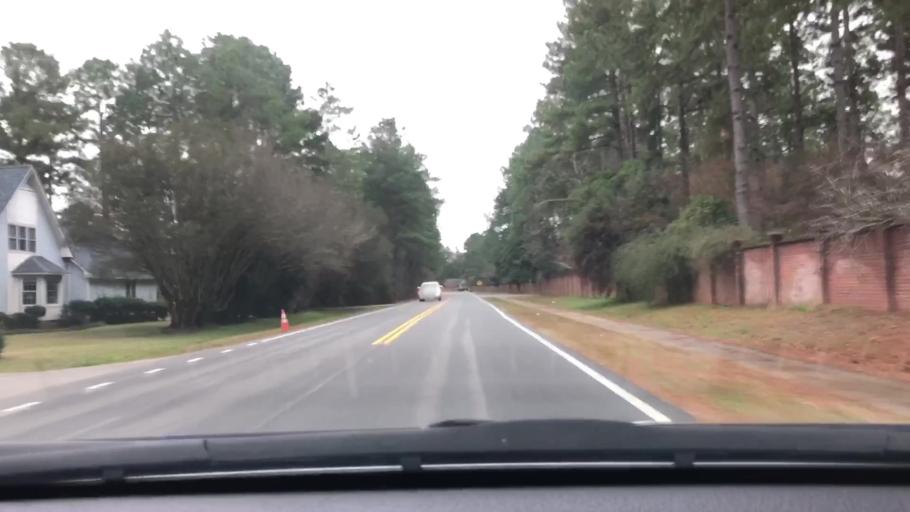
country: US
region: South Carolina
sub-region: Sumter County
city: Cherryvale
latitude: 33.9407
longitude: -80.4044
